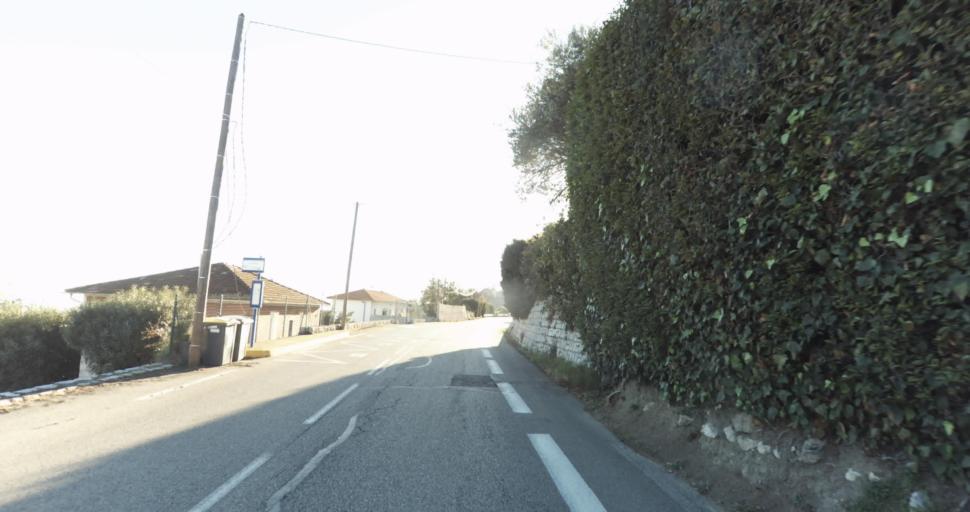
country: FR
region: Provence-Alpes-Cote d'Azur
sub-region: Departement des Alpes-Maritimes
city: Vence
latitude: 43.7338
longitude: 7.1216
